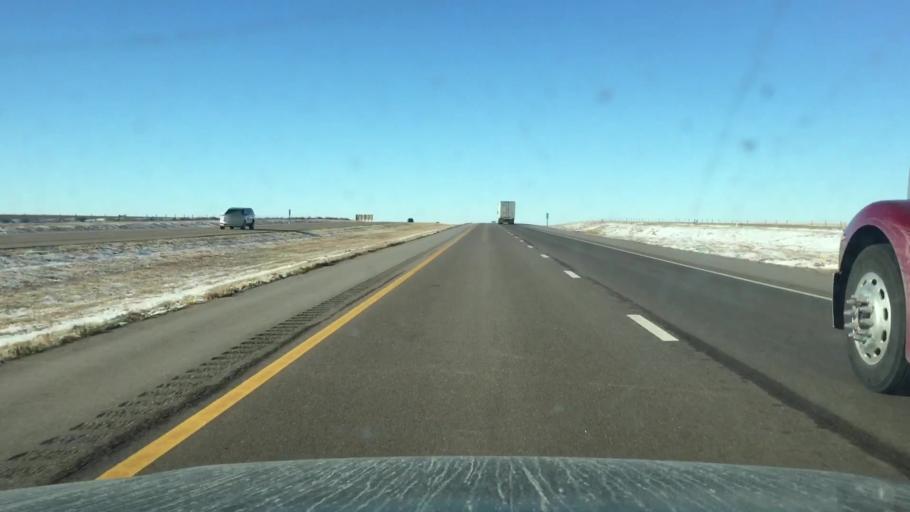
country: US
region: Kansas
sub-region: Logan County
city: Oakley
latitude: 39.1671
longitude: -100.8485
